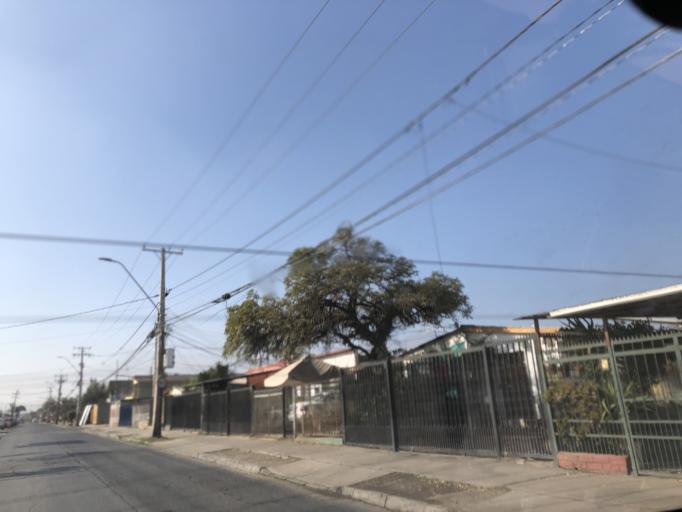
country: CL
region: Santiago Metropolitan
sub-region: Provincia de Cordillera
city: Puente Alto
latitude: -33.6144
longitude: -70.5807
